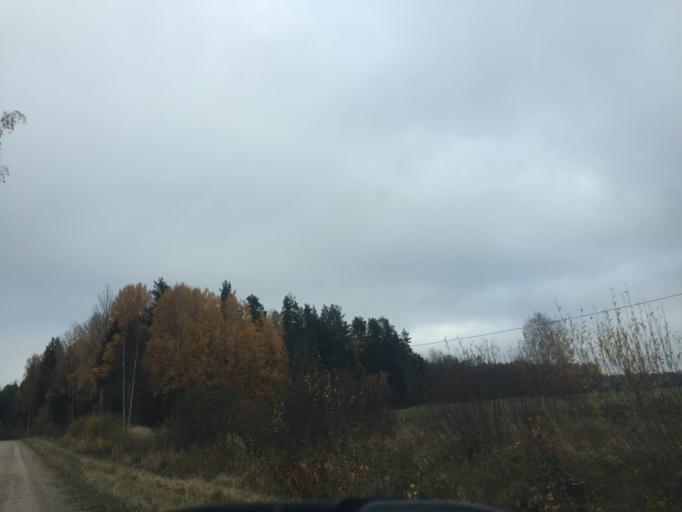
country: LV
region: Jaunpils
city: Jaunpils
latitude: 56.6954
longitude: 23.1166
